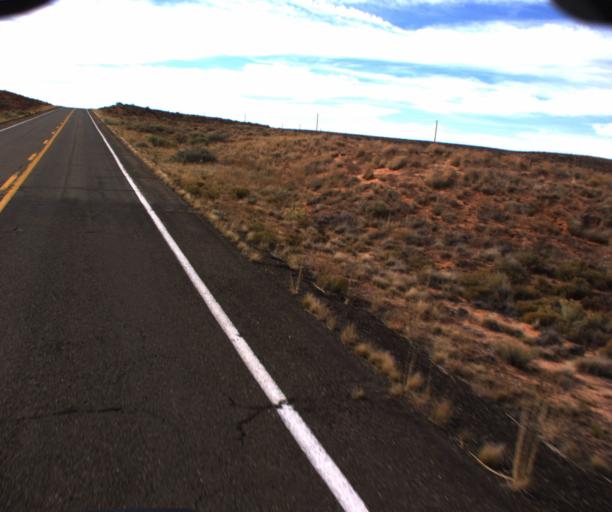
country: US
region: Arizona
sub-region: Coconino County
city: LeChee
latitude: 36.7621
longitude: -111.2852
